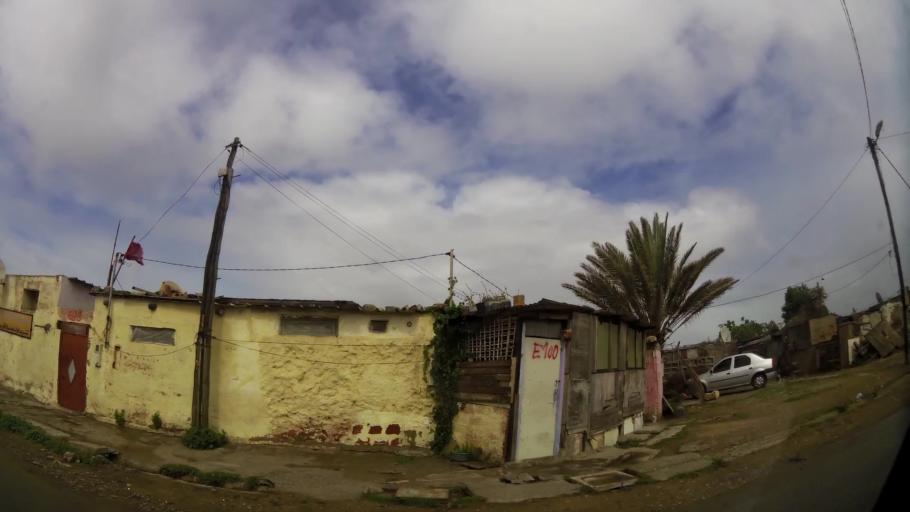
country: MA
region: Grand Casablanca
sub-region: Mohammedia
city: Mohammedia
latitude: 33.6435
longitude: -7.4520
